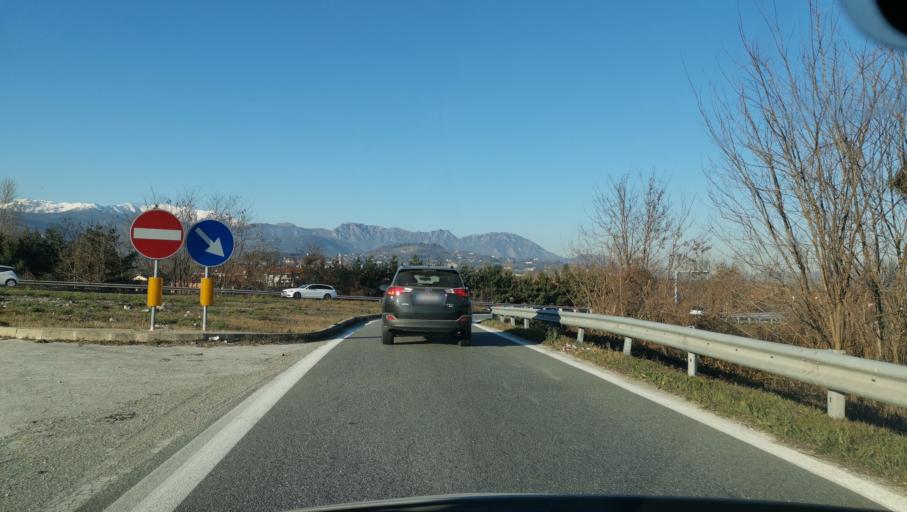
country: IT
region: Piedmont
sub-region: Provincia di Torino
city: Osasco
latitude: 44.8652
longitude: 7.3348
